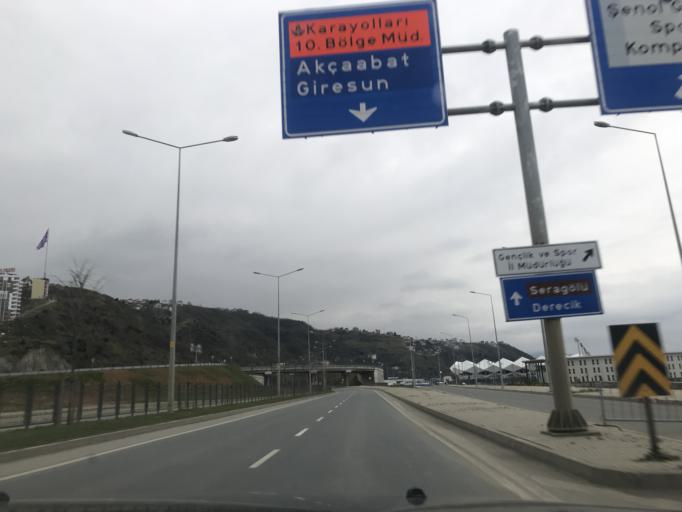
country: TR
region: Trabzon
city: Trabzon
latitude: 40.9960
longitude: 39.6587
